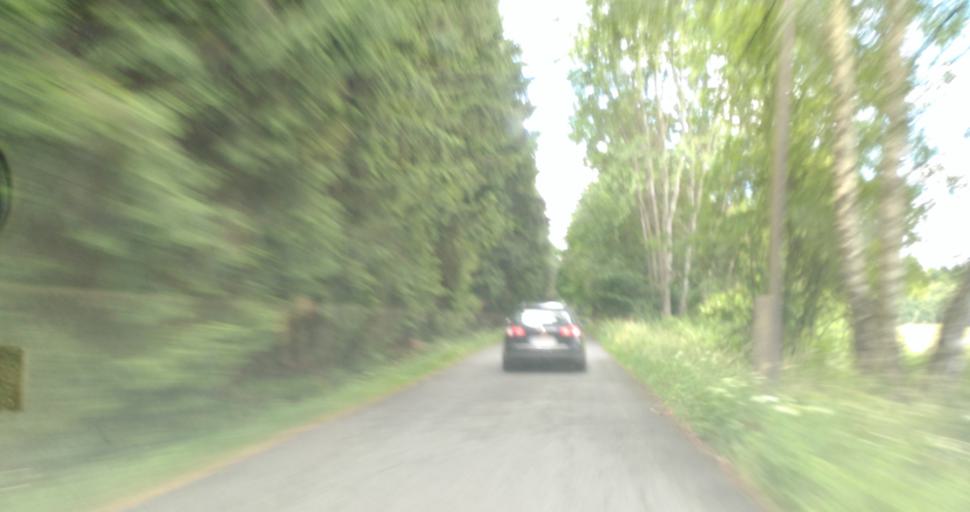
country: CZ
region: Plzensky
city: Zbiroh
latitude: 49.8939
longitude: 13.8073
